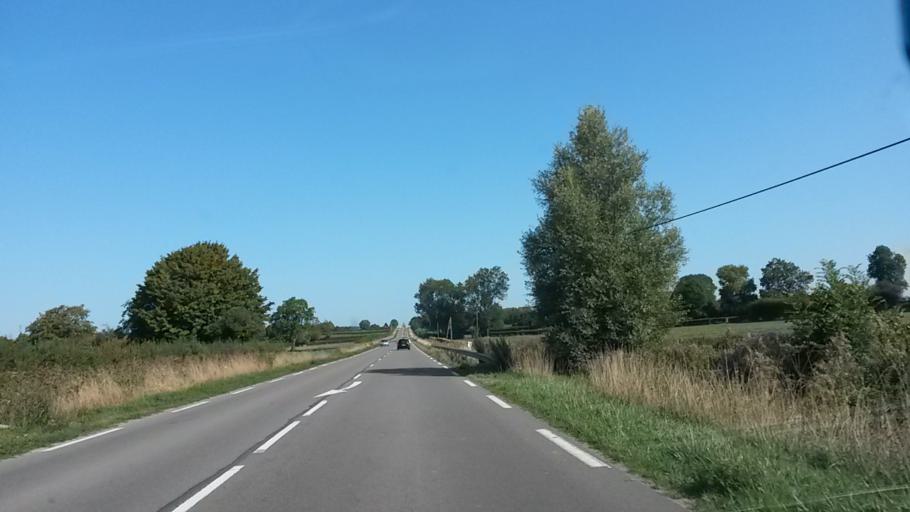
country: FR
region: Nord-Pas-de-Calais
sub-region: Departement du Nord
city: Avesnes-sur-Helpe
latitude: 50.0972
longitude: 3.9307
